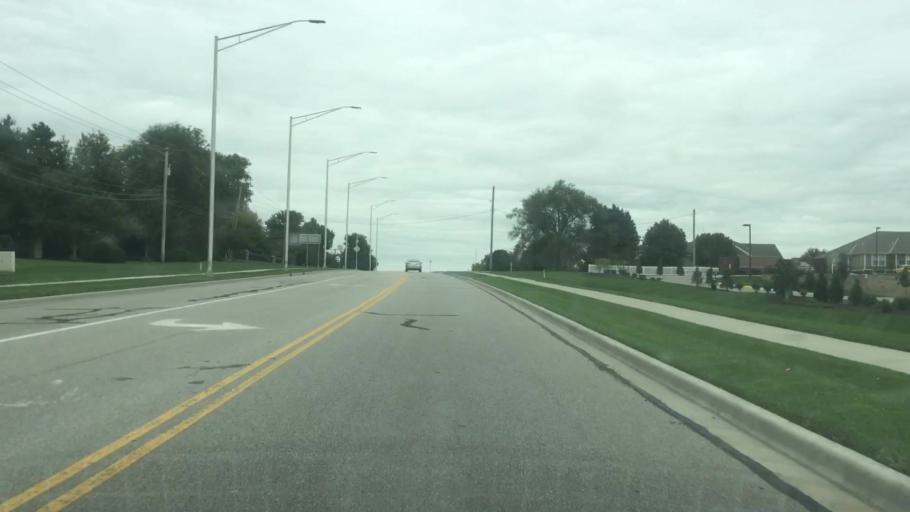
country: US
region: Kansas
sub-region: Johnson County
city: Lenexa
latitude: 38.9773
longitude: -94.7796
